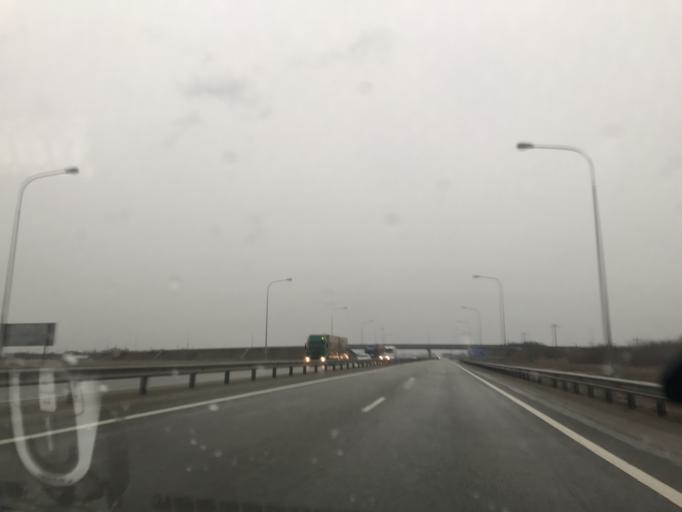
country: RU
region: Krasnodarskiy
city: Pavlovskaya
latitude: 46.2621
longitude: 39.8316
